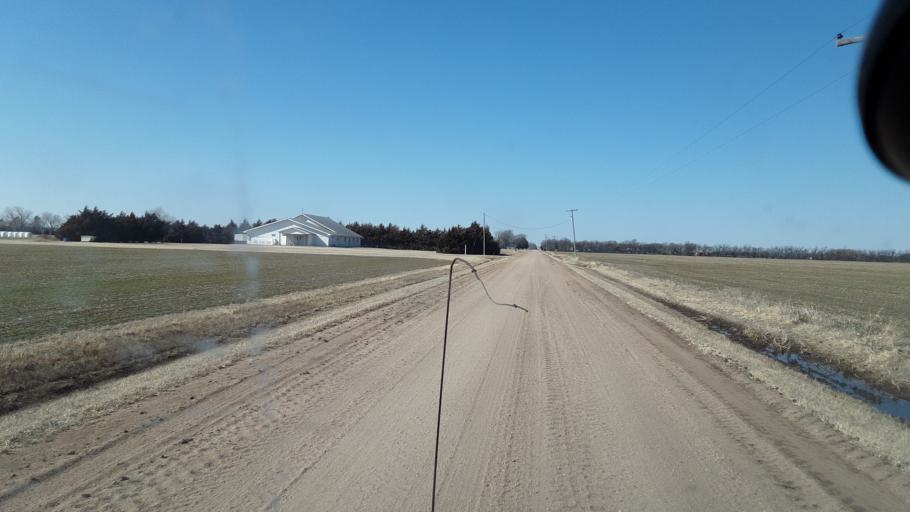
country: US
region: Kansas
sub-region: Reno County
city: South Hutchinson
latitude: 37.9846
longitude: -98.0206
